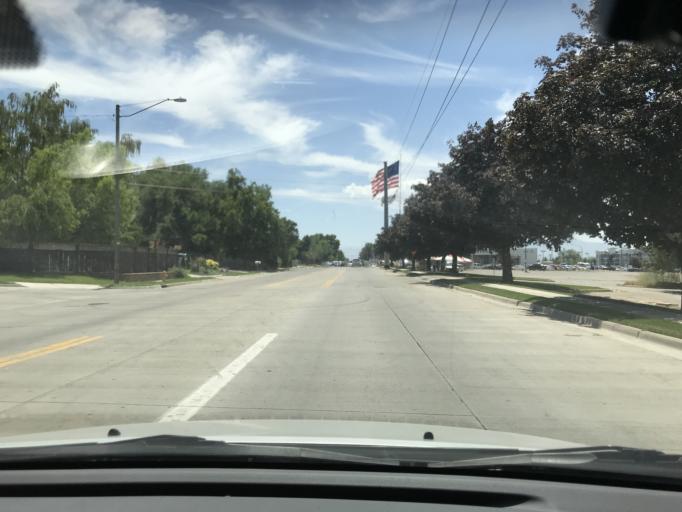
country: US
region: Utah
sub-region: Davis County
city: Woods Cross
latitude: 40.8724
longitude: -111.8877
